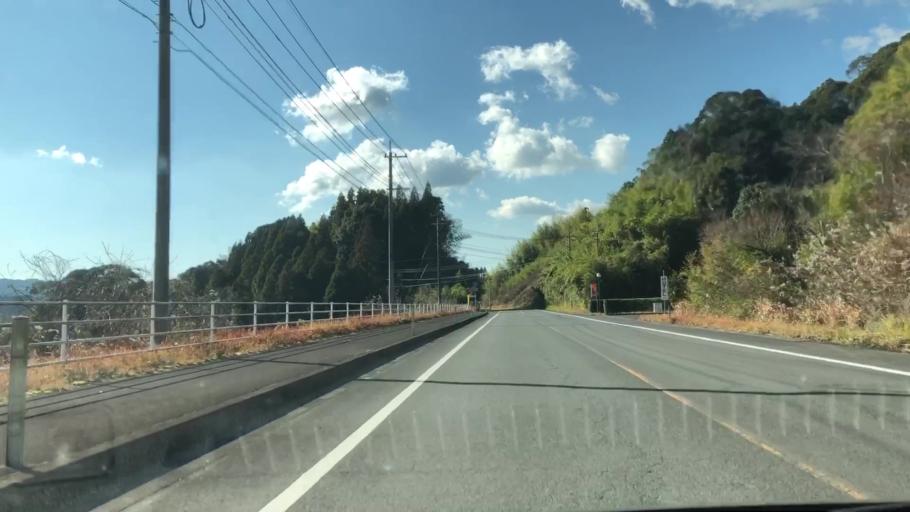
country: JP
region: Kagoshima
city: Satsumasendai
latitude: 31.8627
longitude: 130.3987
